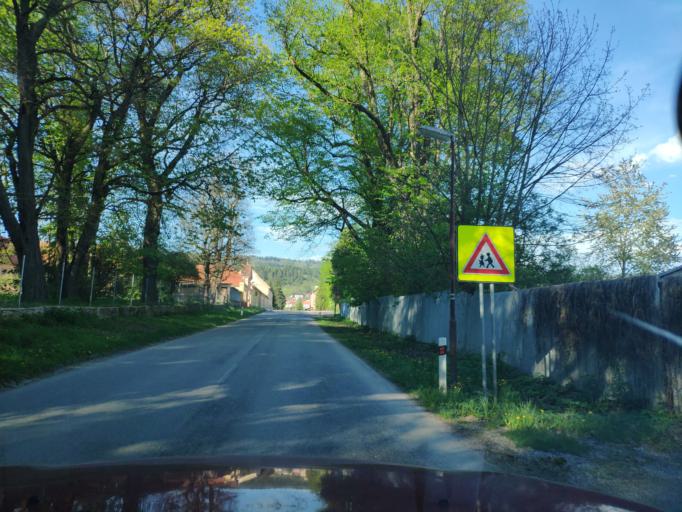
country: SK
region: Presovsky
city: Spisske Podhradie
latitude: 49.0204
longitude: 20.7930
